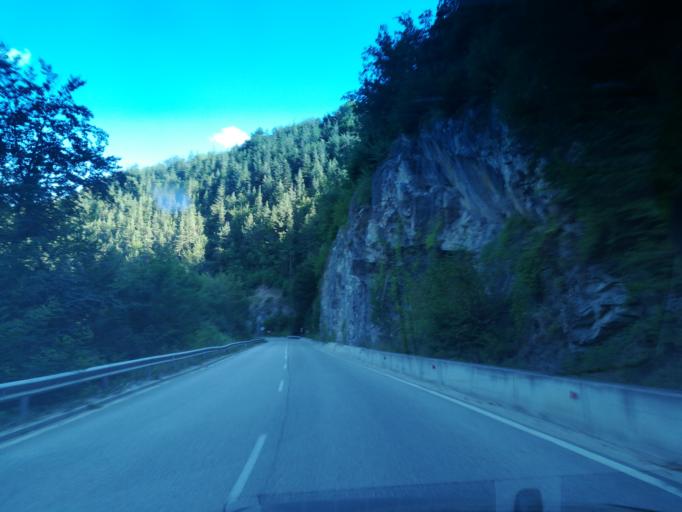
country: BG
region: Smolyan
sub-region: Obshtina Chepelare
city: Chepelare
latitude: 41.8195
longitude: 24.6960
